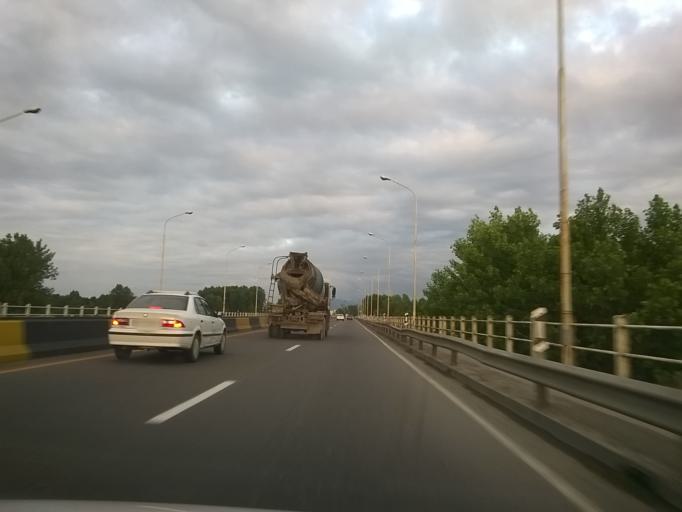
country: IR
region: Gilan
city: Astaneh-ye Ashrafiyeh
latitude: 37.2626
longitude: 49.9248
